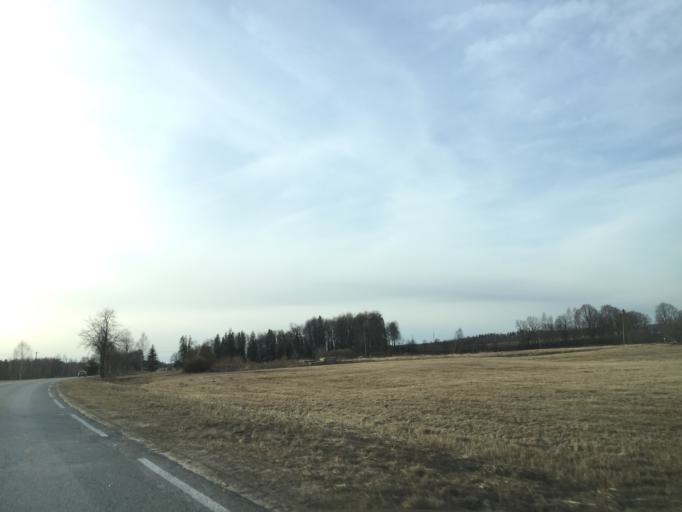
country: LV
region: Krimulda
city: Ragana
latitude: 57.1644
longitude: 24.7539
